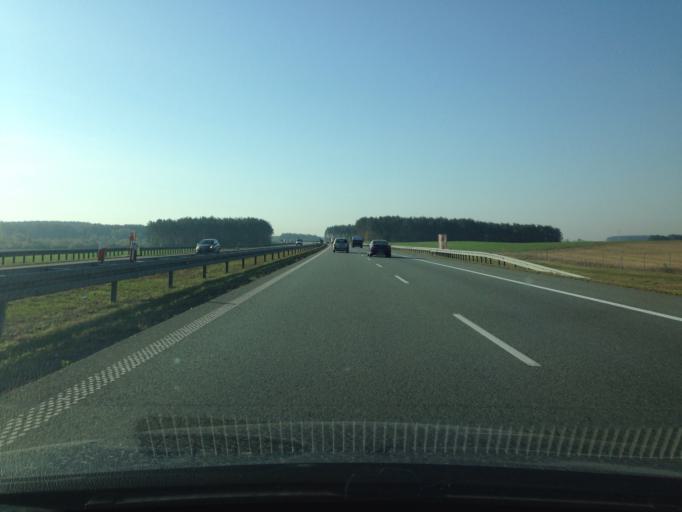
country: PL
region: Pomeranian Voivodeship
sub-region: Powiat tczewski
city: Pelplin
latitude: 54.0083
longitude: 18.6597
